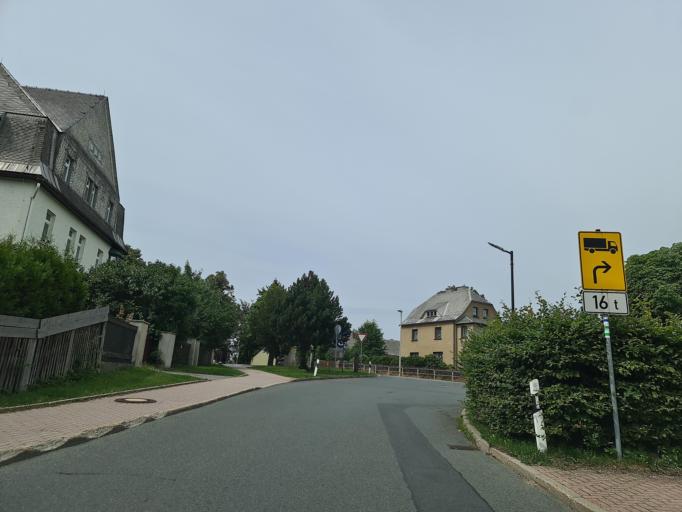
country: DE
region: Saxony
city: Sayda
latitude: 50.7096
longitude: 13.4262
